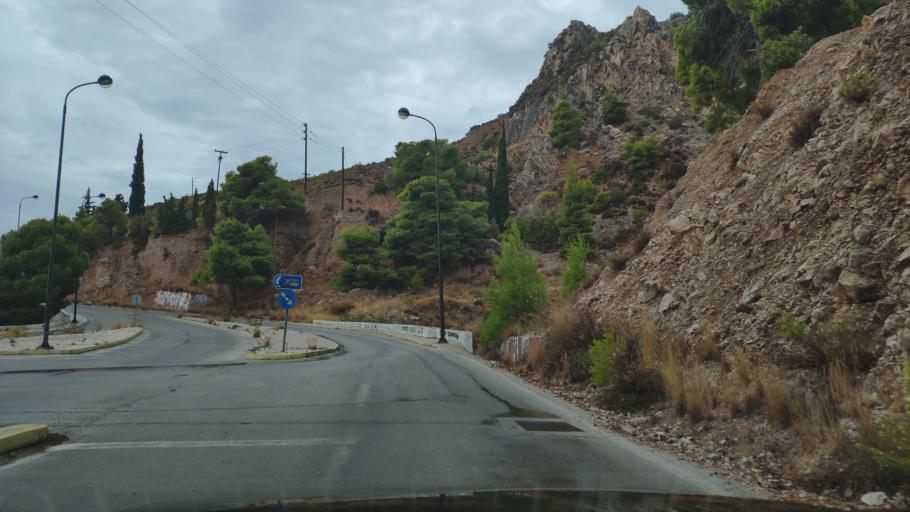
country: GR
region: Peloponnese
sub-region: Nomos Korinthias
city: Loutraki
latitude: 37.9827
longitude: 22.9776
